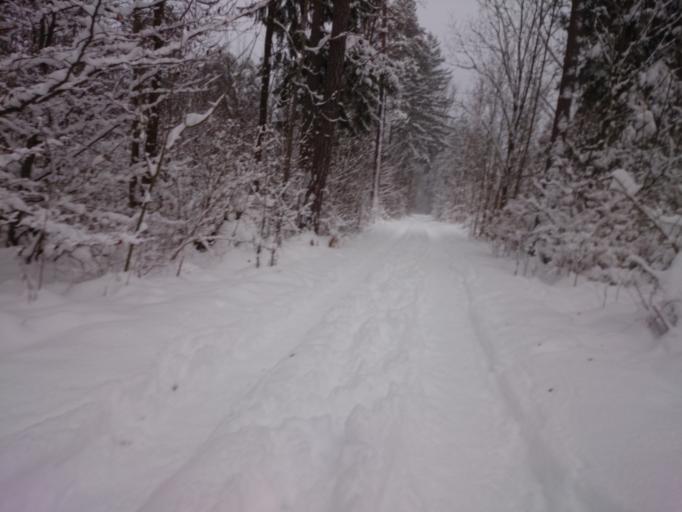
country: DE
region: Bavaria
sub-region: Swabia
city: Konigsbrunn
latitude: 48.2957
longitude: 10.9139
